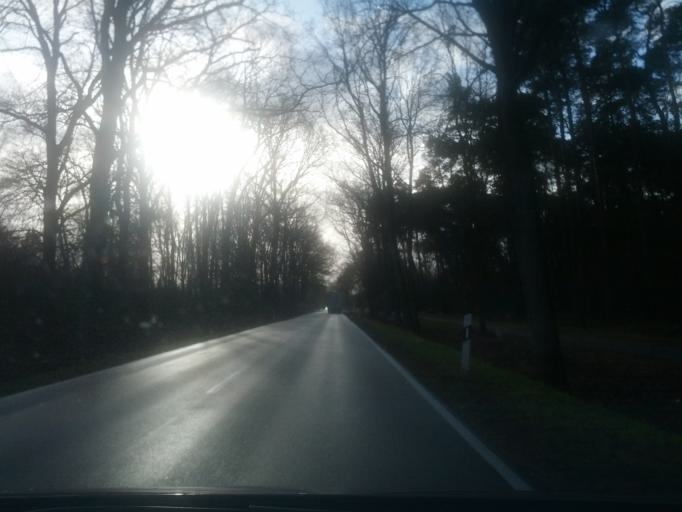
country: DE
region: Lower Saxony
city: Helvesiek
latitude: 53.2229
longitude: 9.4839
